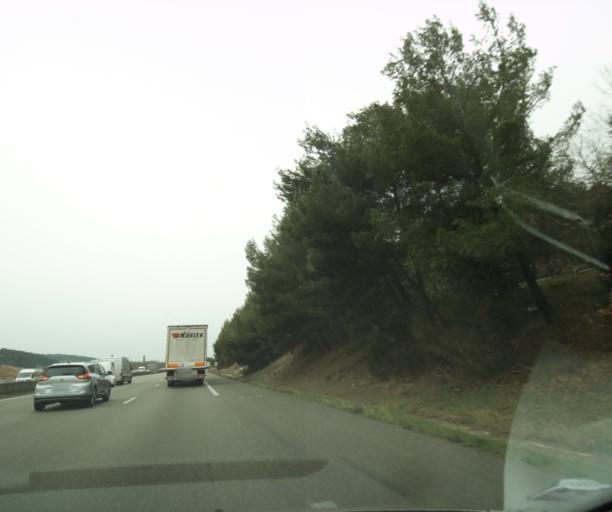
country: FR
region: Provence-Alpes-Cote d'Azur
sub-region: Departement des Bouches-du-Rhone
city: Le Tholonet
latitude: 43.5136
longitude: 5.4886
